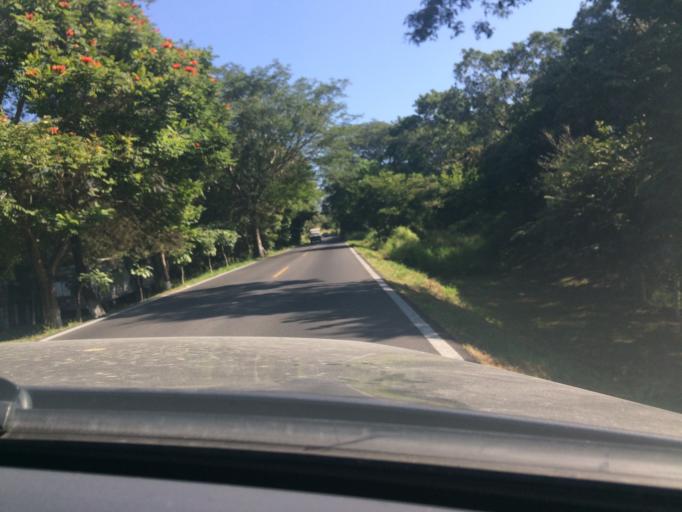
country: MX
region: Colima
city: Suchitlan
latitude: 19.3508
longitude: -103.7345
